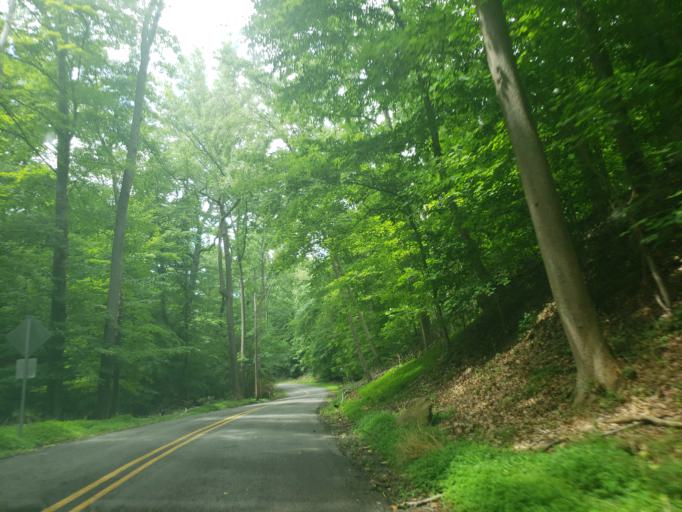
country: US
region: Pennsylvania
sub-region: Allegheny County
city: Coraopolis
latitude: 40.5386
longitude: -80.1341
